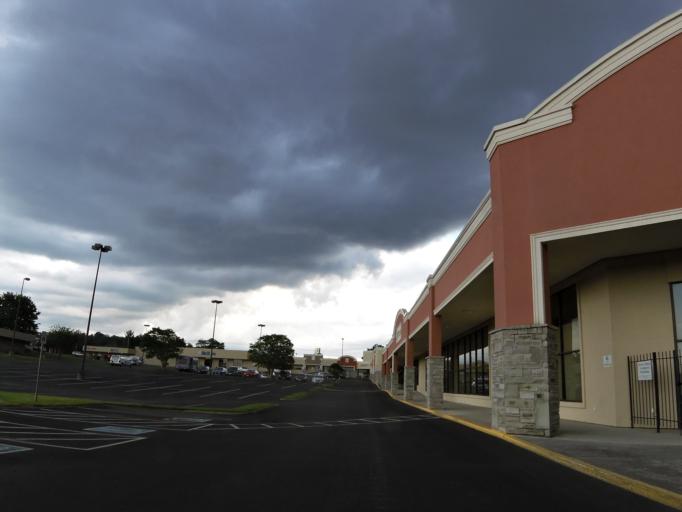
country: US
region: Tennessee
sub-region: Blount County
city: Louisville
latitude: 35.9206
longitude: -84.0524
